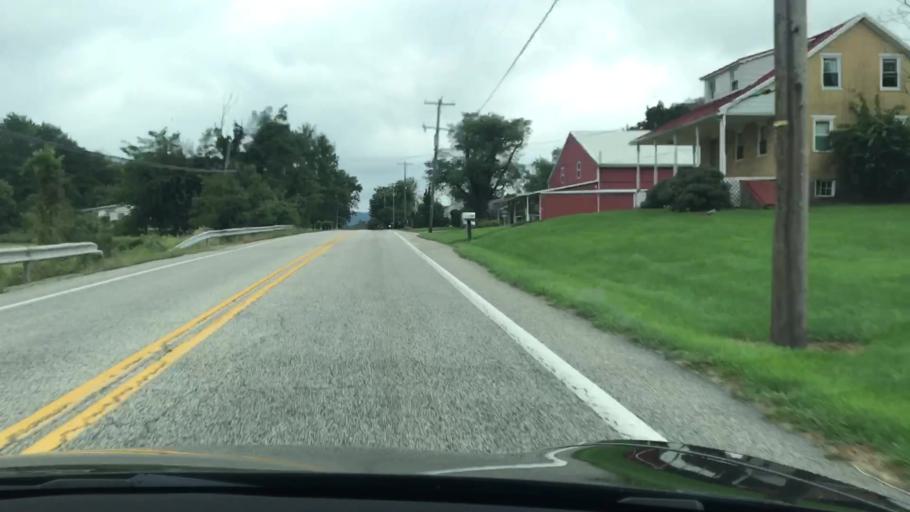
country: US
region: Pennsylvania
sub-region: Cumberland County
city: Shiremanstown
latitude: 40.1515
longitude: -76.9667
